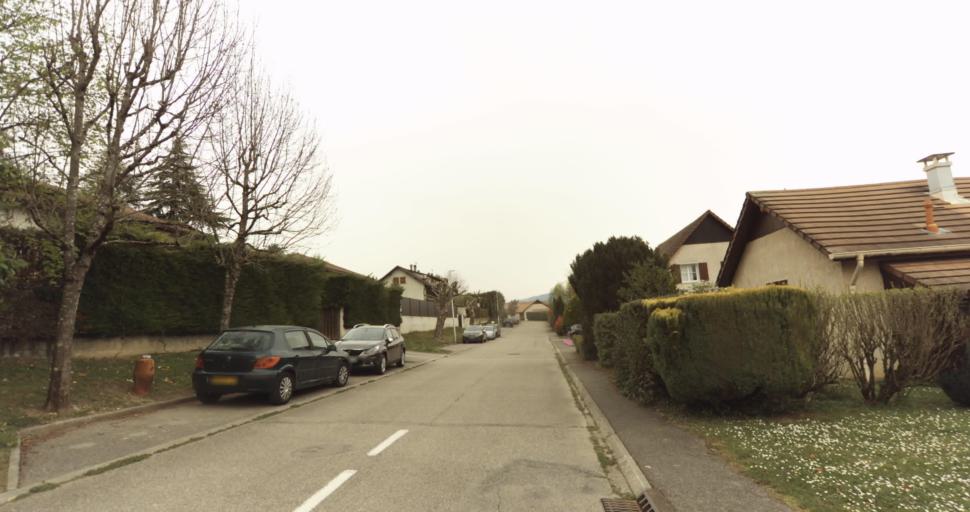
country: FR
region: Rhone-Alpes
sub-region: Departement de l'Isere
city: Biviers
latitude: 45.2334
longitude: 5.8102
